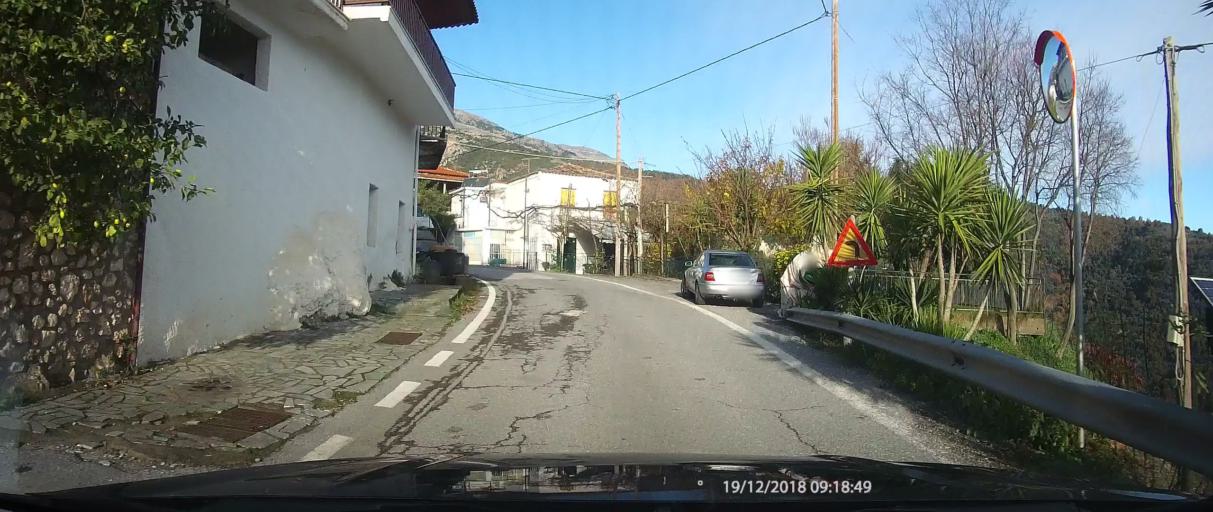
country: GR
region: Peloponnese
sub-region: Nomos Lakonias
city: Magoula
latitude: 37.0934
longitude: 22.3499
